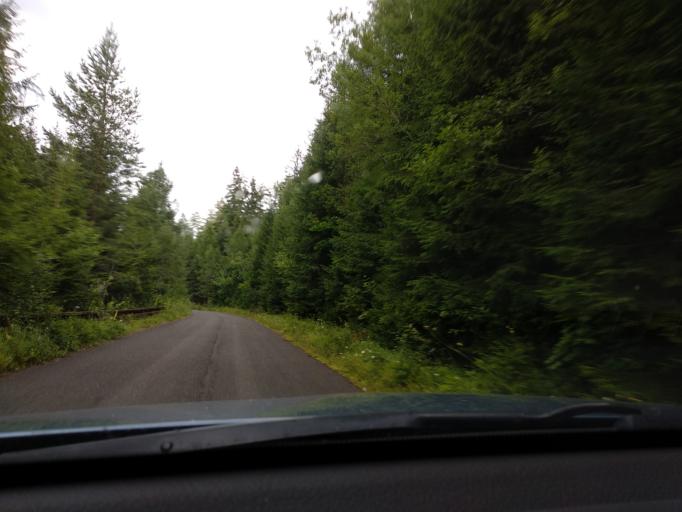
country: SK
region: Zilinsky
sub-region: Okres Liptovsky Mikulas
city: Hybe
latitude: 49.0245
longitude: 19.8895
